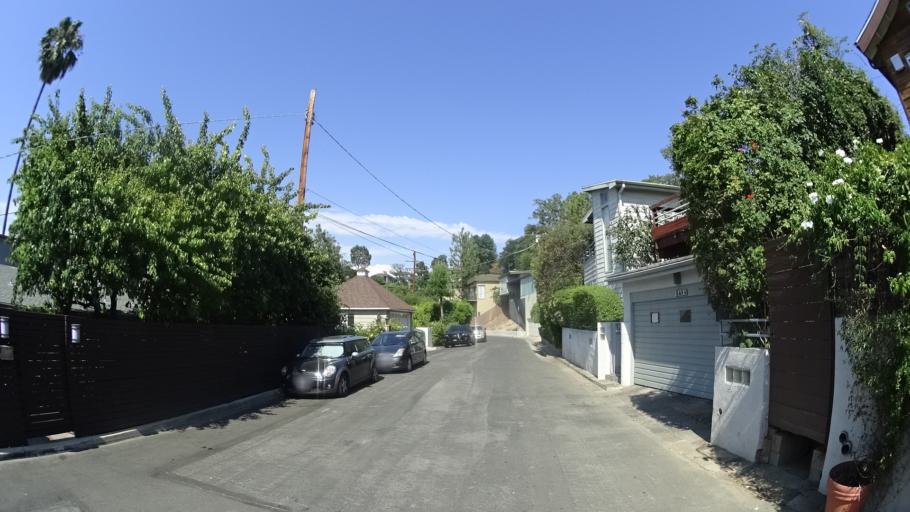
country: US
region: California
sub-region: Los Angeles County
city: Universal City
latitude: 34.1356
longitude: -118.3799
